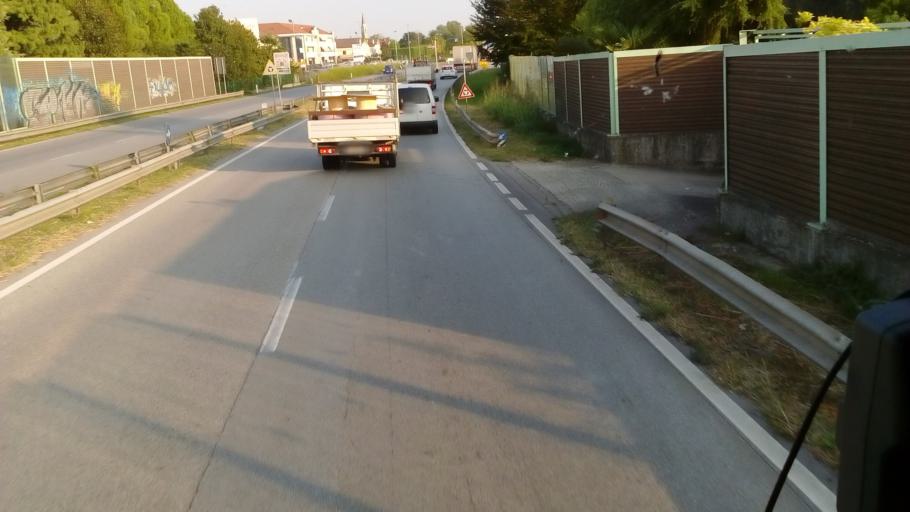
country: IT
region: Veneto
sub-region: Provincia di Padova
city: Villatora
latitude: 45.3875
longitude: 11.9592
